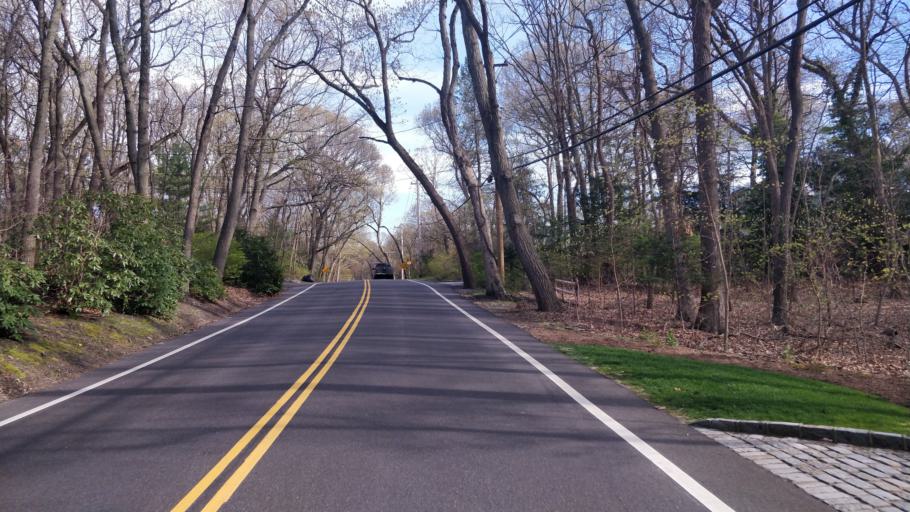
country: US
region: New York
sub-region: Suffolk County
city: Stony Brook
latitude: 40.9455
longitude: -73.1371
